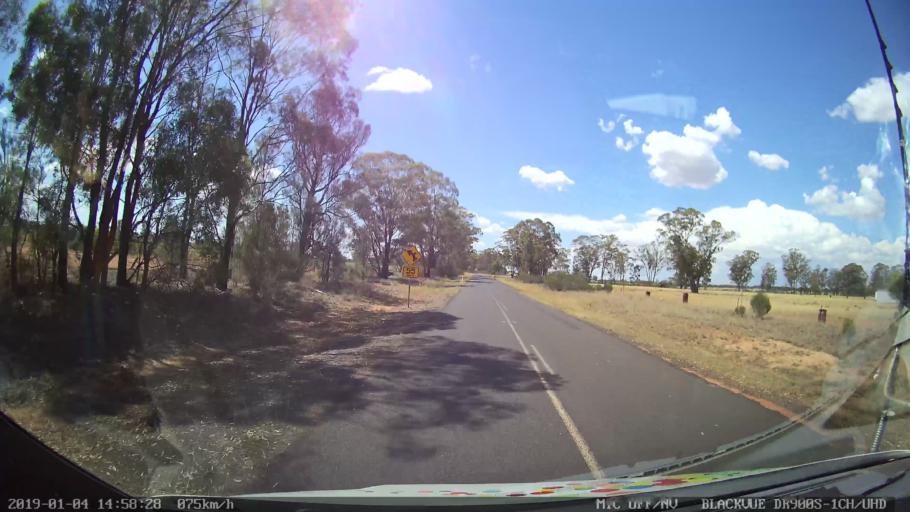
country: AU
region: New South Wales
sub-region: Gilgandra
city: Gilgandra
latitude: -31.9553
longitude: 148.6321
